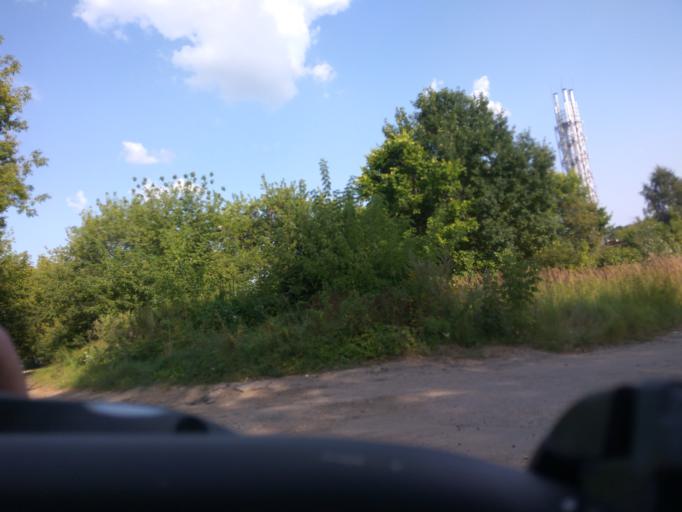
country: RU
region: Moscow
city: Orekhovo-Borisovo Severnoye
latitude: 55.6162
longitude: 37.6673
